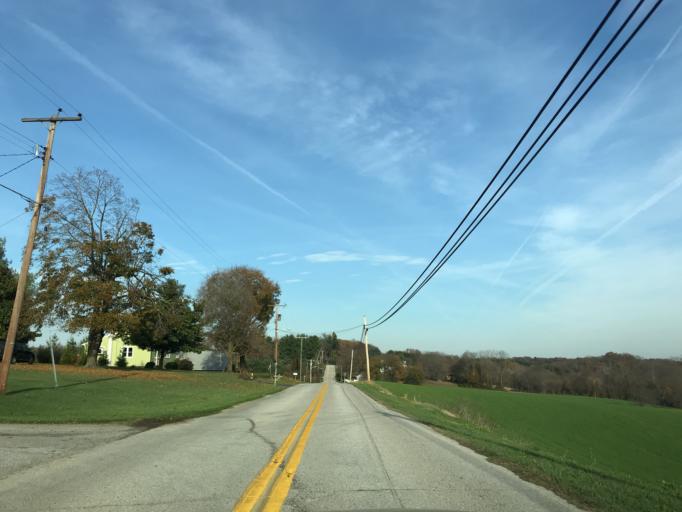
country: US
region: Maryland
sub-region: Baltimore County
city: Reisterstown
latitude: 39.5342
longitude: -76.8200
